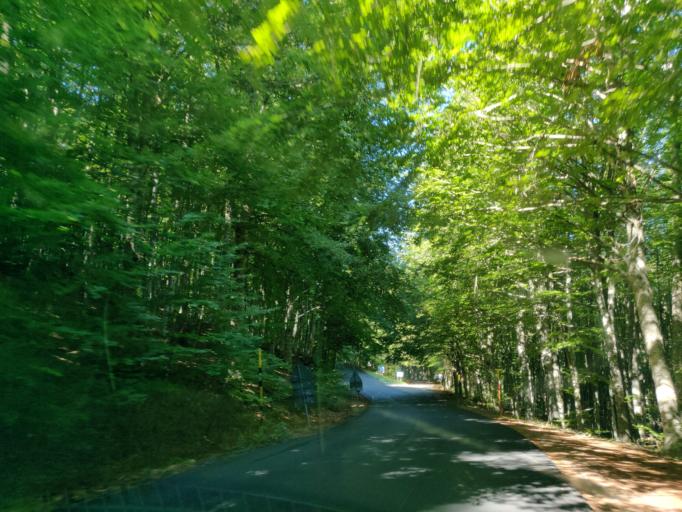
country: IT
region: Tuscany
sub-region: Provincia di Siena
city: Abbadia San Salvatore
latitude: 42.9037
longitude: 11.6201
